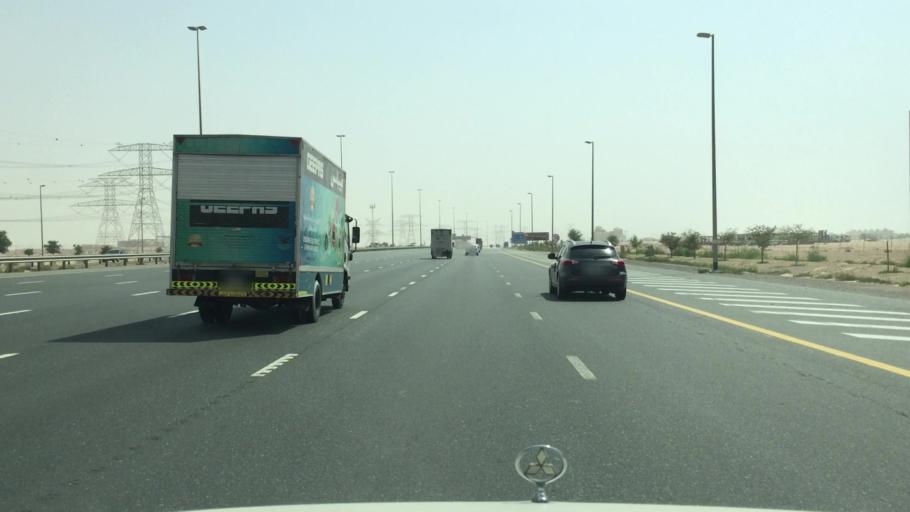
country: AE
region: Dubai
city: Dubai
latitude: 25.0808
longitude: 55.3824
